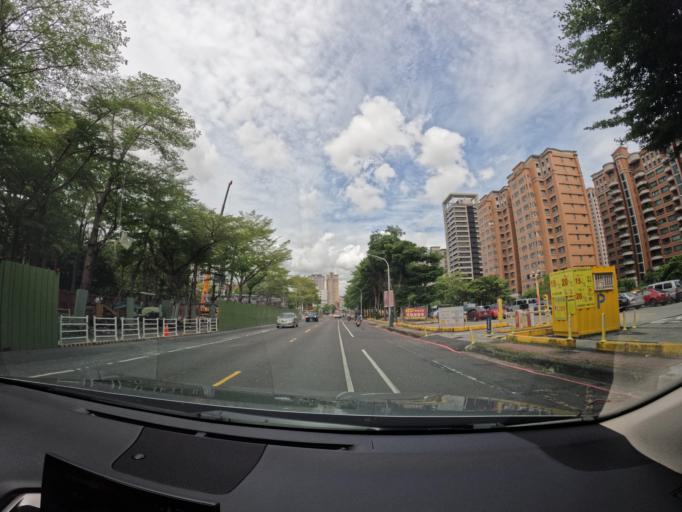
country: TW
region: Kaohsiung
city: Kaohsiung
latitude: 22.6549
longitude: 120.2866
